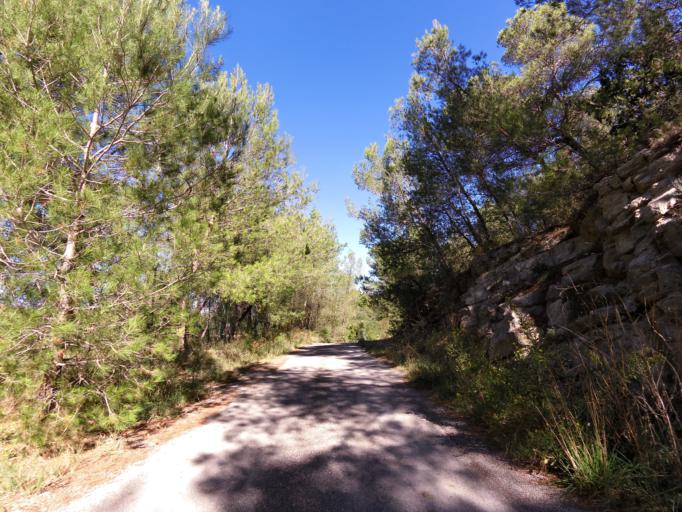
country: FR
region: Languedoc-Roussillon
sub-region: Departement du Gard
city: Aubais
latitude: 43.7481
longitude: 4.1414
